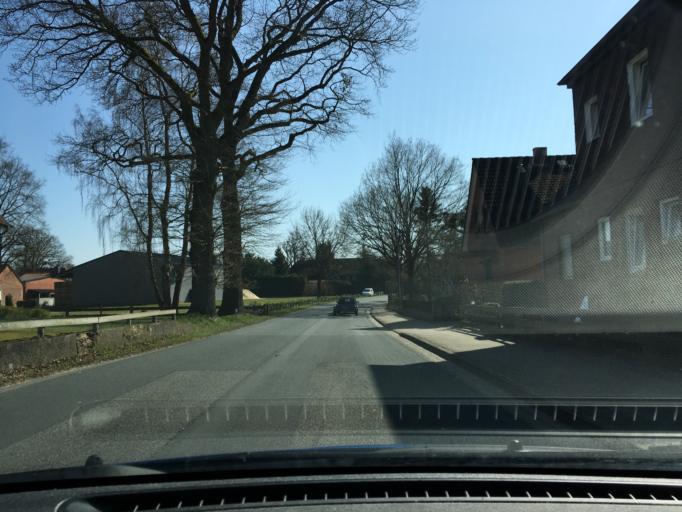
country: DE
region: Lower Saxony
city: Wriedel
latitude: 53.0340
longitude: 10.2992
